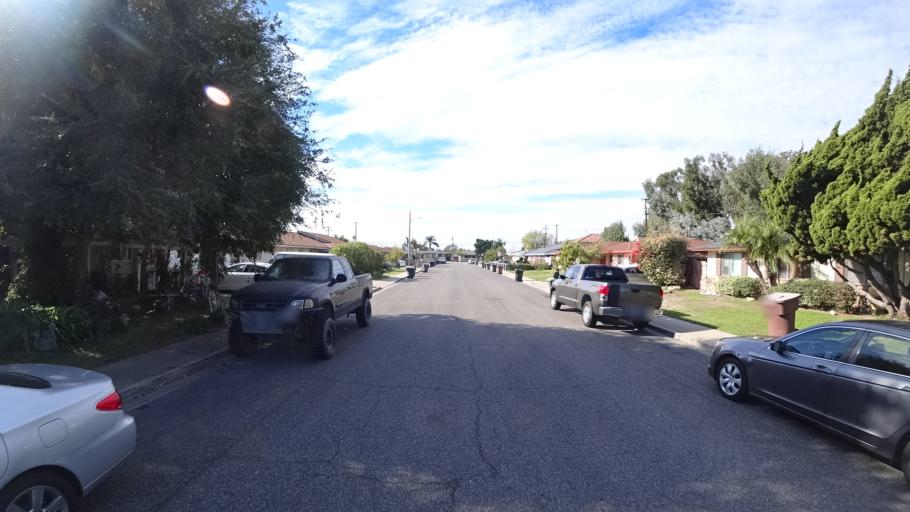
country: US
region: California
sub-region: Orange County
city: Garden Grove
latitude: 33.7804
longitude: -117.9179
